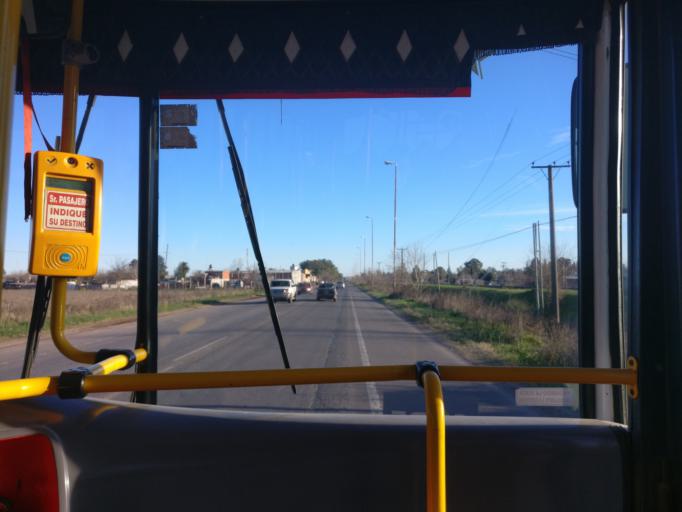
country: AR
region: Buenos Aires
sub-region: Partido de Ezeiza
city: Ezeiza
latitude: -34.9294
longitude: -58.6142
